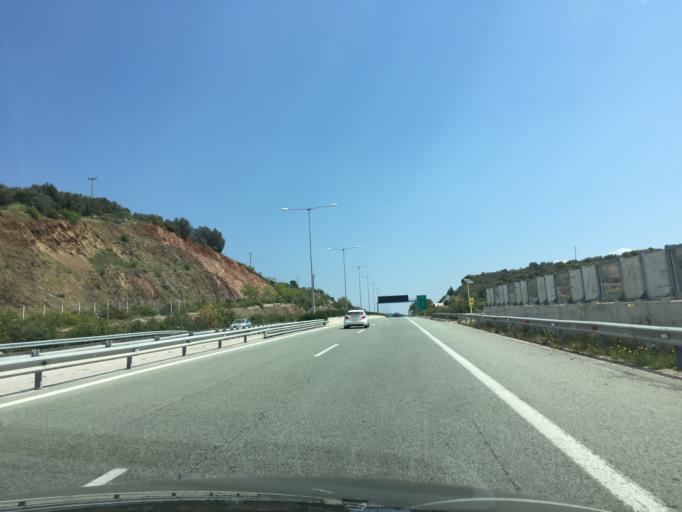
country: GR
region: Central Greece
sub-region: Nomos Fthiotidos
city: Pelasgia
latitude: 38.8852
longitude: 22.7779
